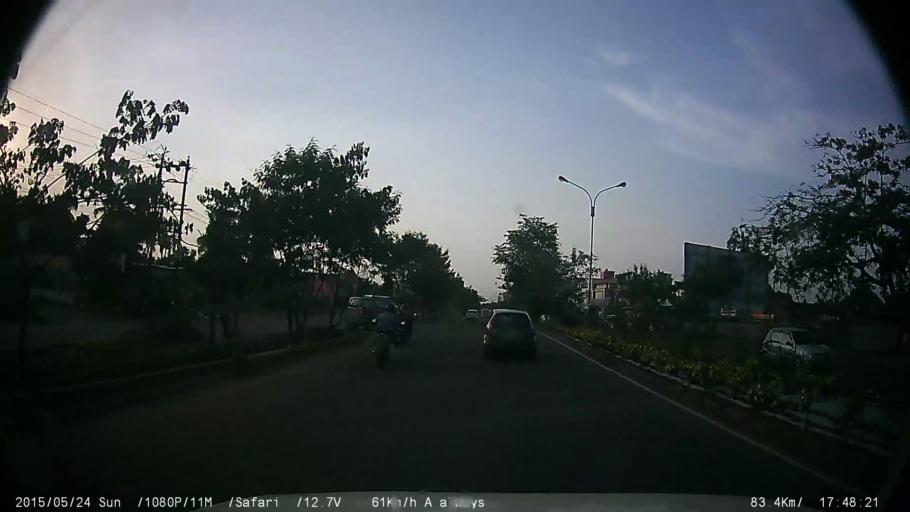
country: IN
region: Kerala
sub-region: Ernakulam
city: Cochin
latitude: 9.9809
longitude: 76.3169
